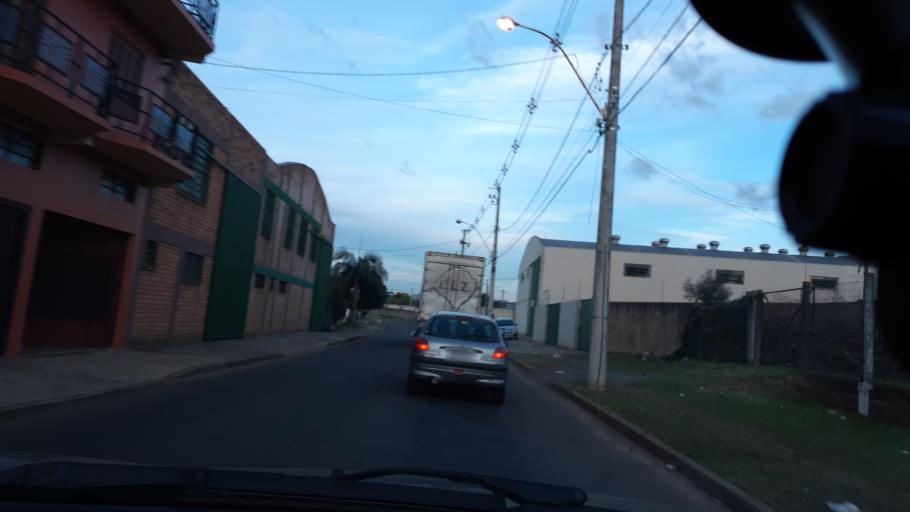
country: BR
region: Rio Grande do Sul
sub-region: Sapucaia Do Sul
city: Sapucaia
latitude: -29.8445
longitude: -51.1493
